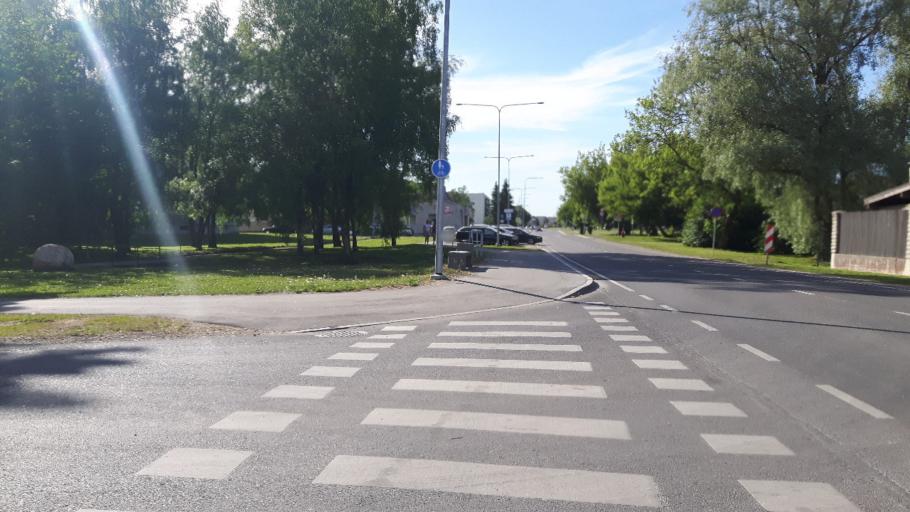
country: EE
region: Harju
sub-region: Joelaehtme vald
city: Loo
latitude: 59.4335
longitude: 24.9489
